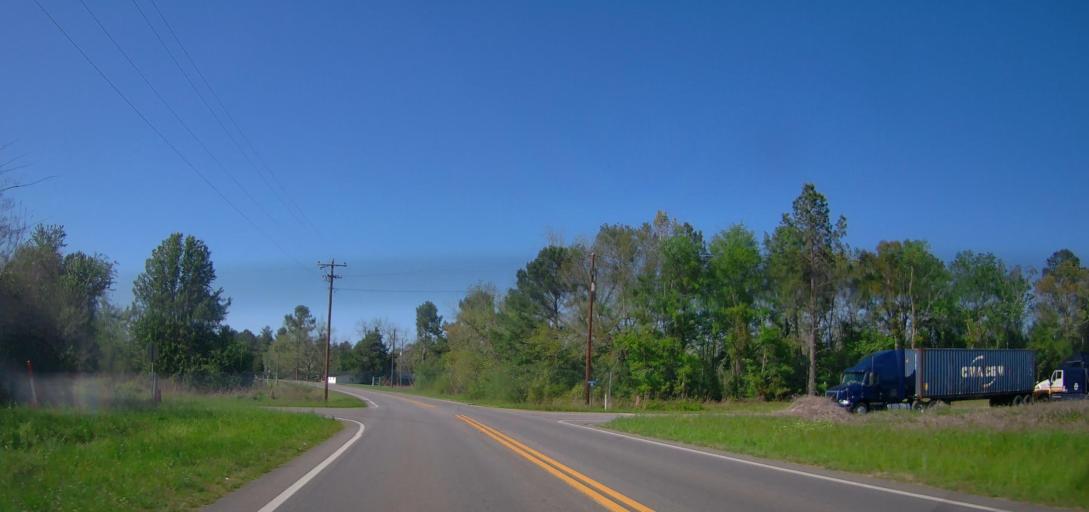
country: US
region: Georgia
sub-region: Pulaski County
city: Hawkinsville
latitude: 32.1282
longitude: -83.5005
